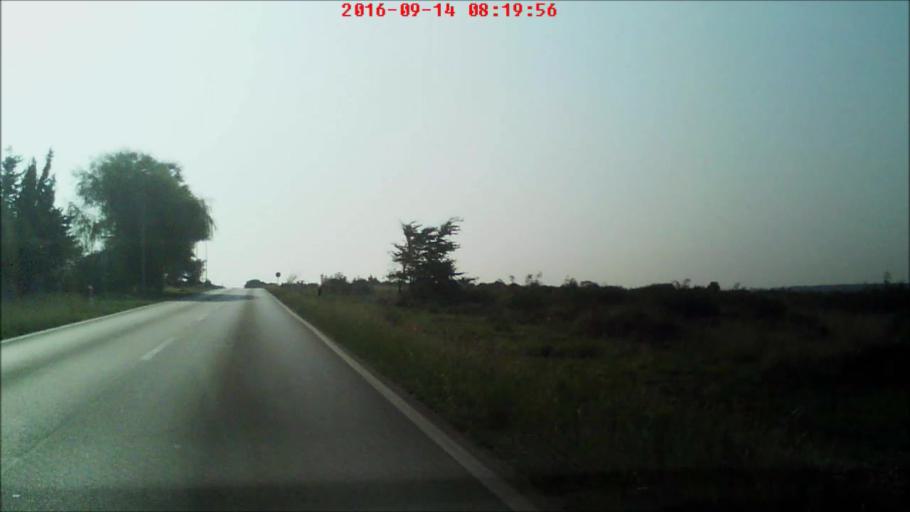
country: HR
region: Zadarska
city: Nin
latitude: 44.2293
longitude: 15.1955
